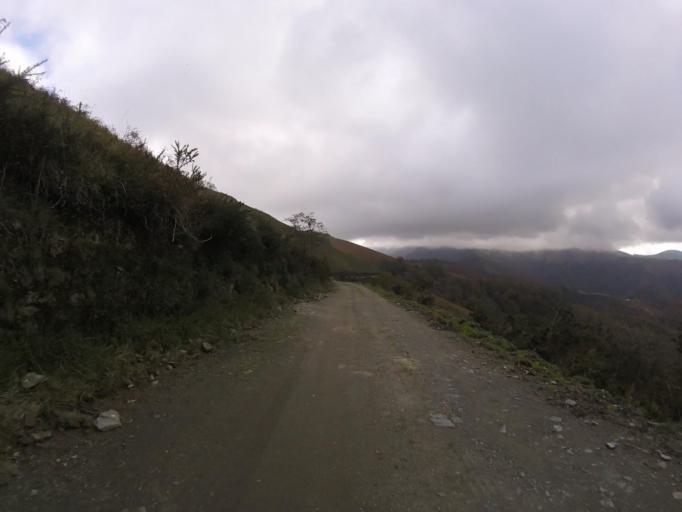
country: ES
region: Navarre
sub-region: Provincia de Navarra
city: Goizueta
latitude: 43.1958
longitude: -1.8203
